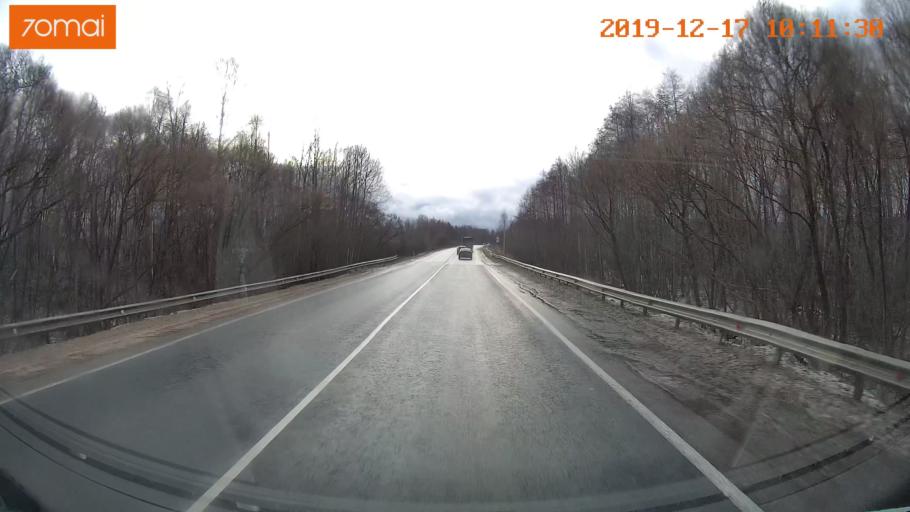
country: RU
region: Vladimir
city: Anopino
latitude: 55.8235
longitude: 40.6571
